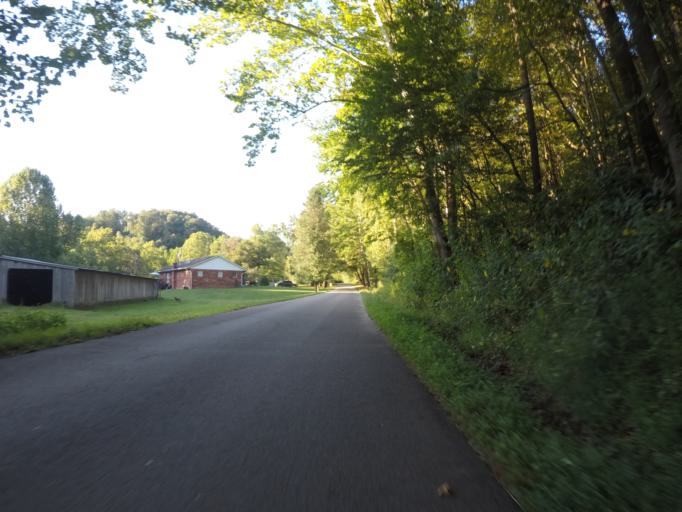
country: US
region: Ohio
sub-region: Lawrence County
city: Coal Grove
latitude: 38.5572
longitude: -82.5531
